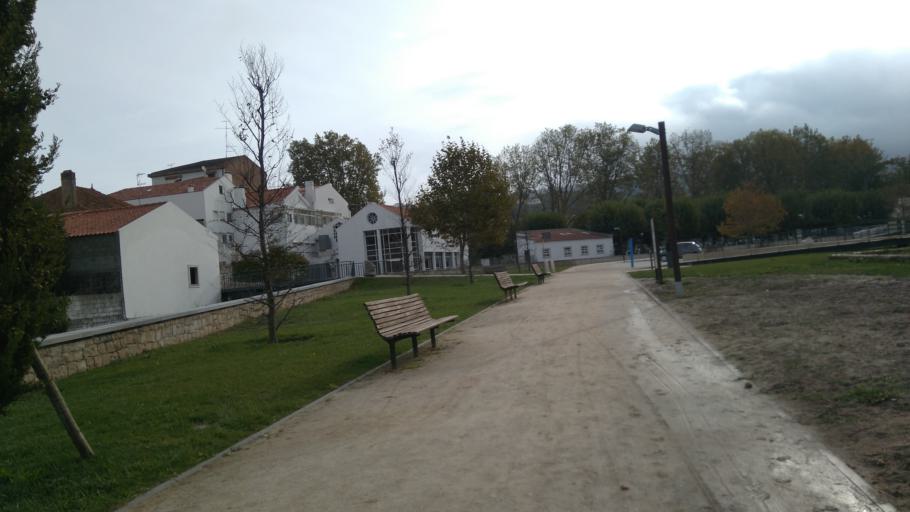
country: PT
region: Leiria
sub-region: Porto de Mos
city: Porto de Mos
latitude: 39.5991
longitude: -8.8213
